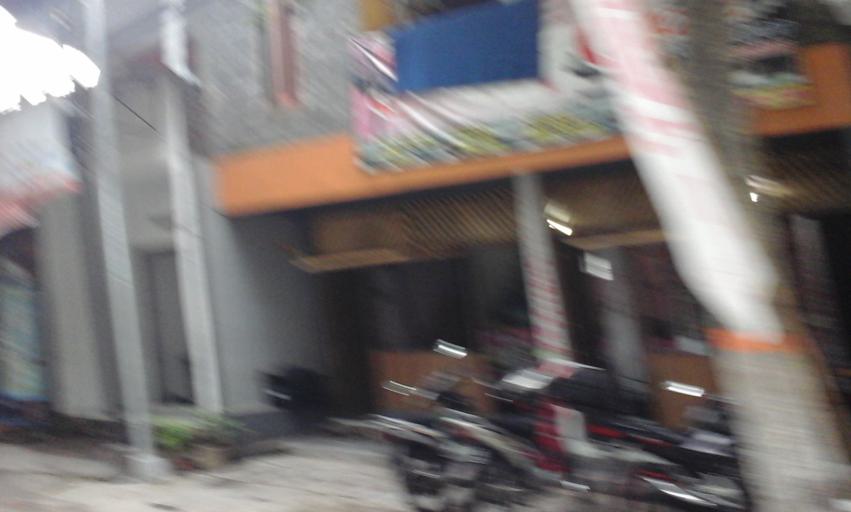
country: ID
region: East Java
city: Rogotrunan
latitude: -8.1176
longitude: 113.2269
